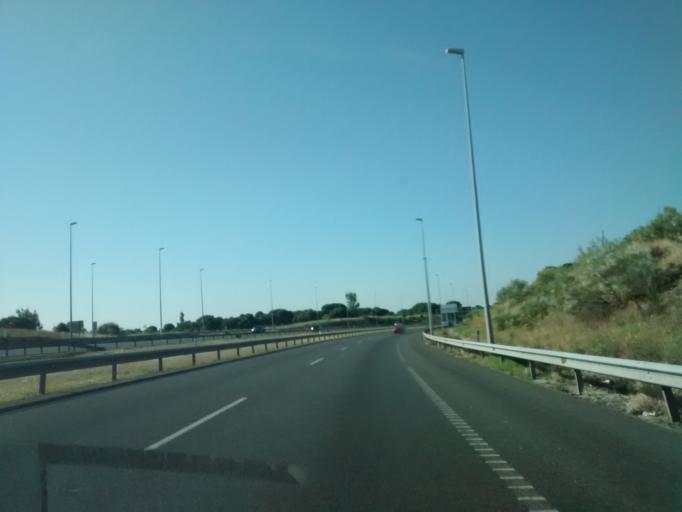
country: ES
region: Madrid
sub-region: Provincia de Madrid
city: Majadahonda
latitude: 40.4423
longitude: -3.8781
